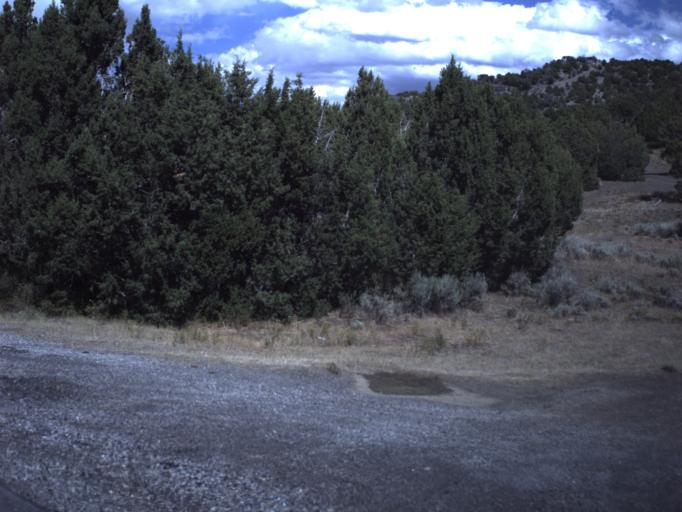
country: US
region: Utah
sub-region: Tooele County
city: Grantsville
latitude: 40.3380
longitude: -112.5682
